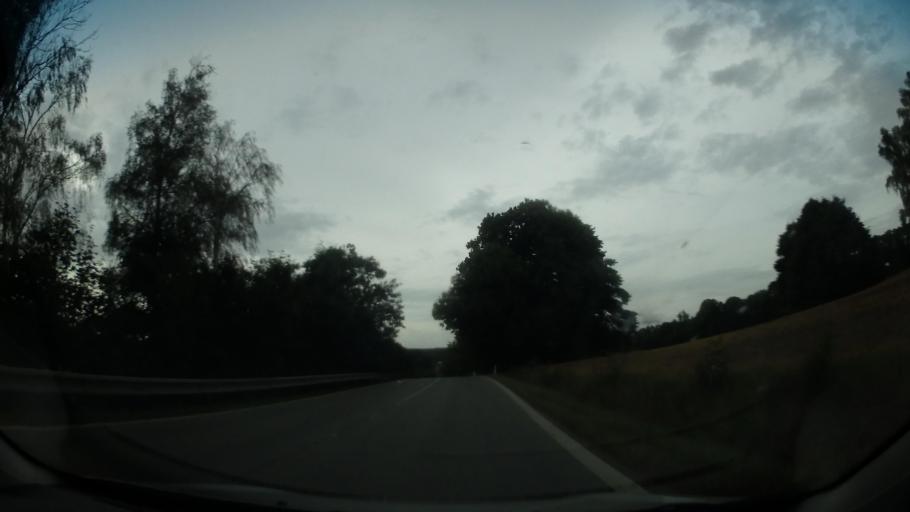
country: CZ
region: Vysocina
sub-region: Okres Zd'ar nad Sazavou
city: Nove Mesto na Morave
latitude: 49.5607
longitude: 16.0440
